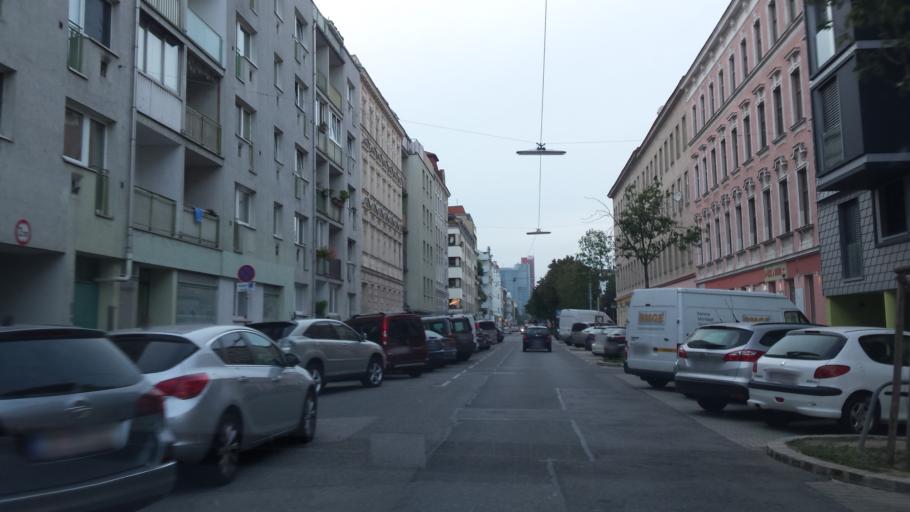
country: AT
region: Vienna
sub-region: Wien Stadt
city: Vienna
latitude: 48.2246
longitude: 16.4253
